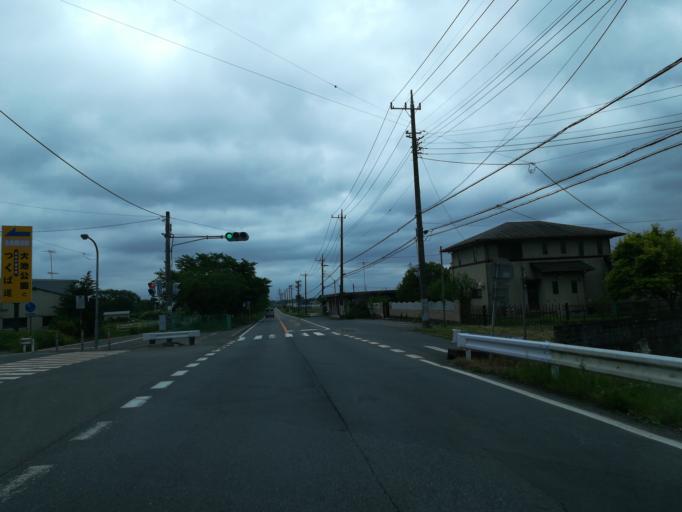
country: JP
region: Ibaraki
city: Tsukuba
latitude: 36.1877
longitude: 140.0792
